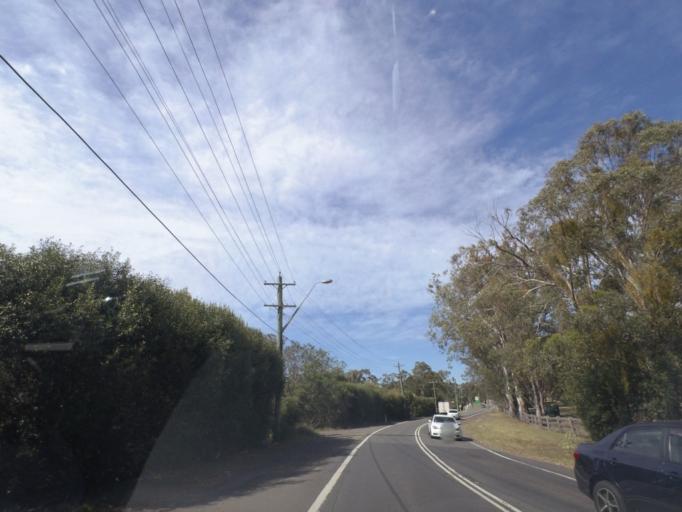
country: AU
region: New South Wales
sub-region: Campbelltown Municipality
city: Denham Court
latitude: -33.9842
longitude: 150.8446
